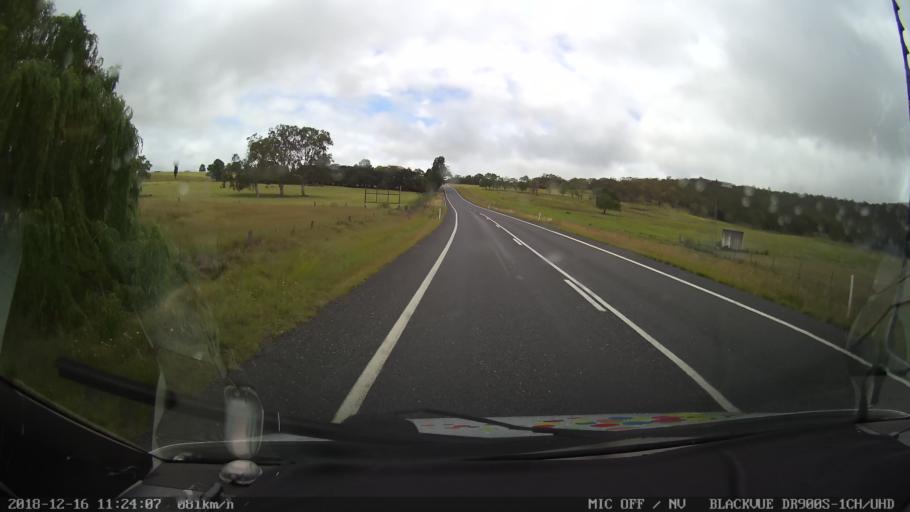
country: AU
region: New South Wales
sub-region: Tenterfield Municipality
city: Carrolls Creek
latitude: -29.0571
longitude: 152.0436
